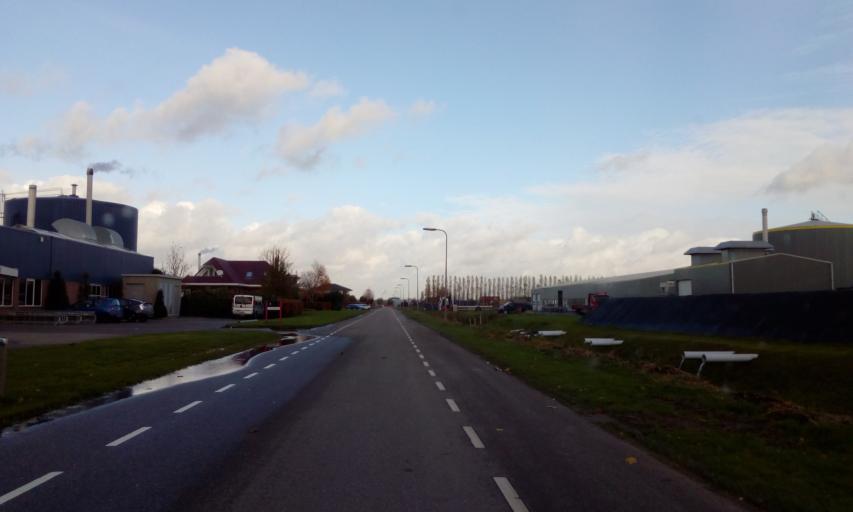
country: NL
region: South Holland
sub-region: Gemeente Lansingerland
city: Bleiswijk
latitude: 52.0138
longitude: 4.5166
